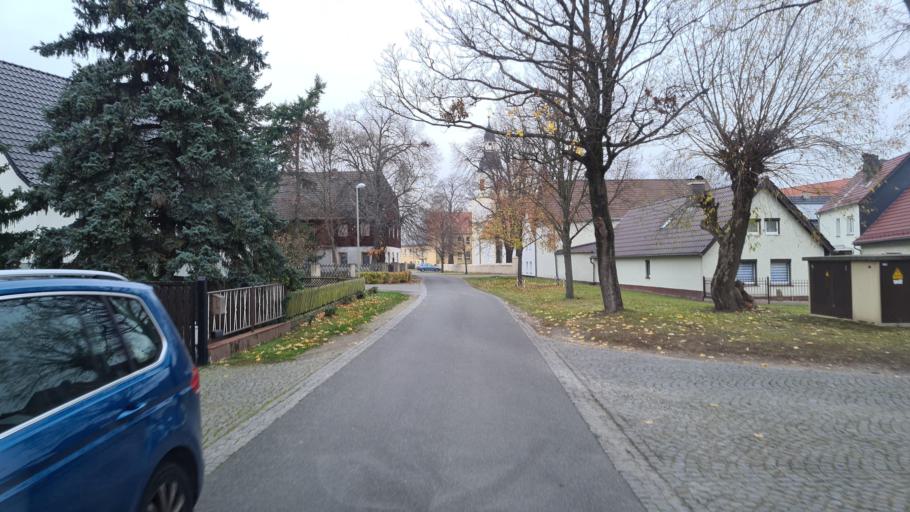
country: DE
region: Brandenburg
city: Groden
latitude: 51.4072
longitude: 13.5718
